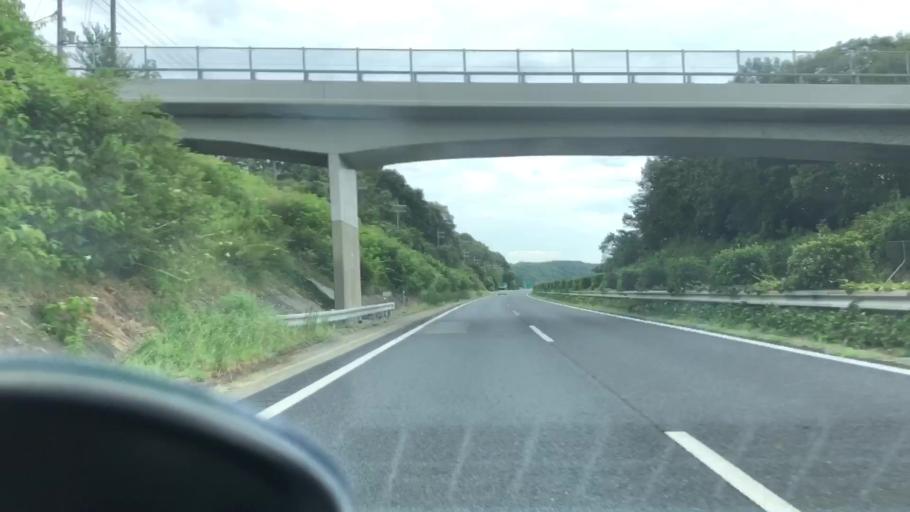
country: JP
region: Hyogo
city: Yashiro
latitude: 34.9303
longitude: 134.9770
